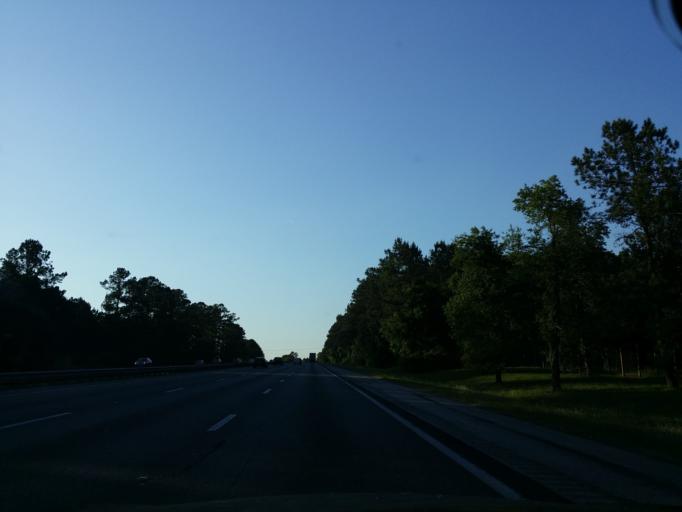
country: US
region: Florida
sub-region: Alachua County
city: Alachua
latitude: 29.7316
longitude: -82.4740
